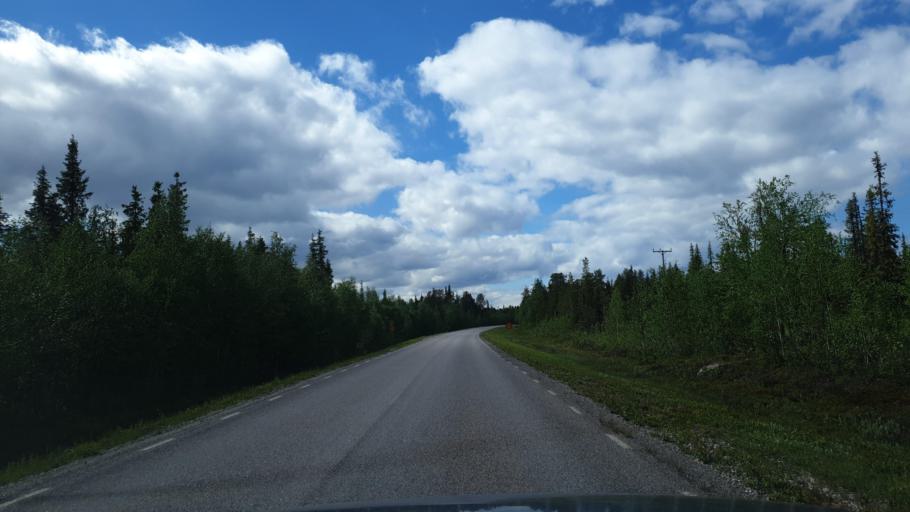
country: SE
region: Norrbotten
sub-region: Jokkmokks Kommun
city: Jokkmokk
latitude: 67.1038
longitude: 19.7195
